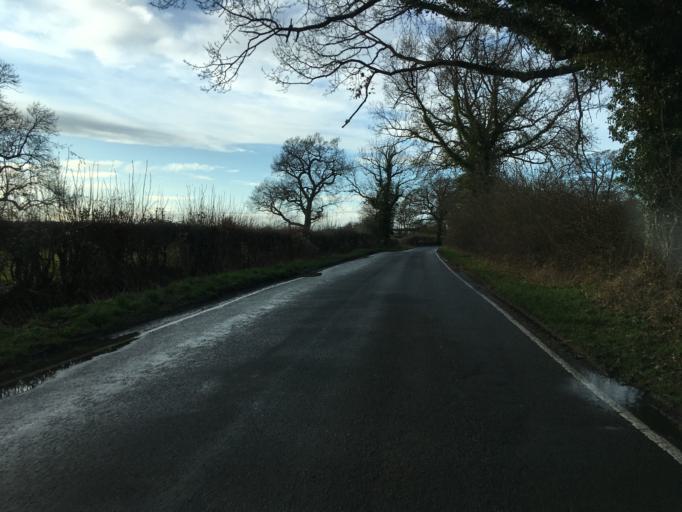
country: GB
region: England
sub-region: Warwickshire
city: Alcester
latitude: 52.2252
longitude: -1.8185
